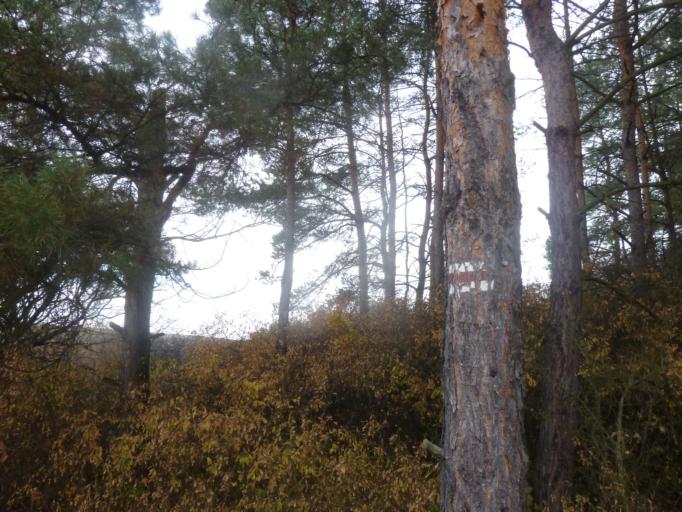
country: HU
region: Nograd
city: Kazar
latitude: 48.0312
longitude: 19.8350
